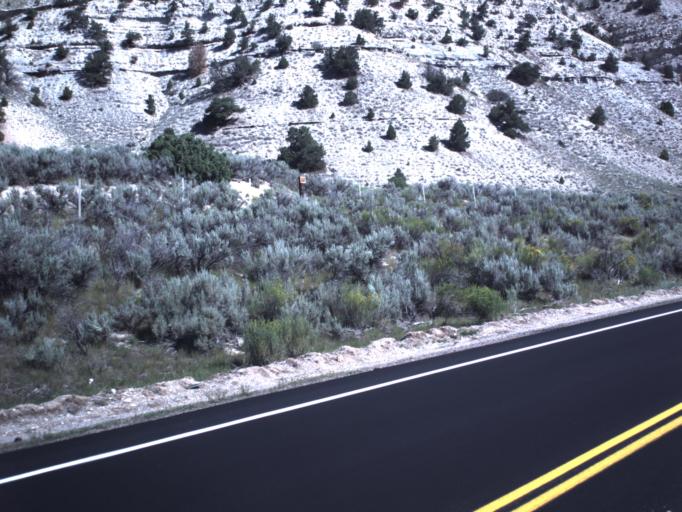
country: US
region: Utah
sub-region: Duchesne County
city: Duchesne
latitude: 39.9694
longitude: -110.6327
